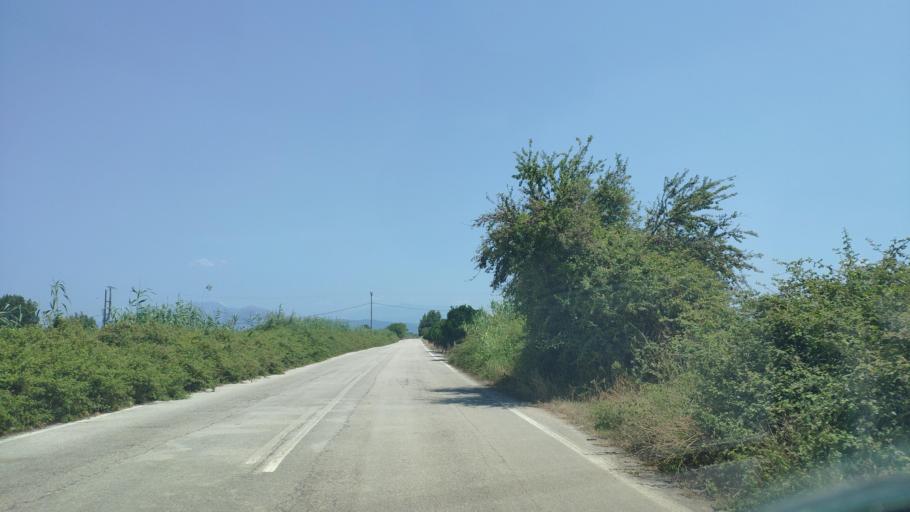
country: GR
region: Epirus
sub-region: Nomos Artas
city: Aneza
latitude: 39.0640
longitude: 20.8744
